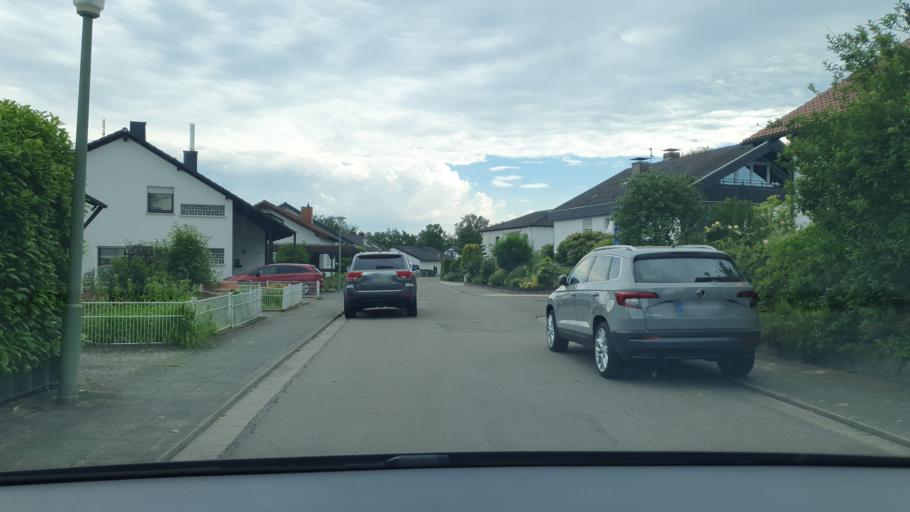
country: DE
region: Rheinland-Pfalz
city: Kaiserslautern
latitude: 49.4659
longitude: 7.7682
